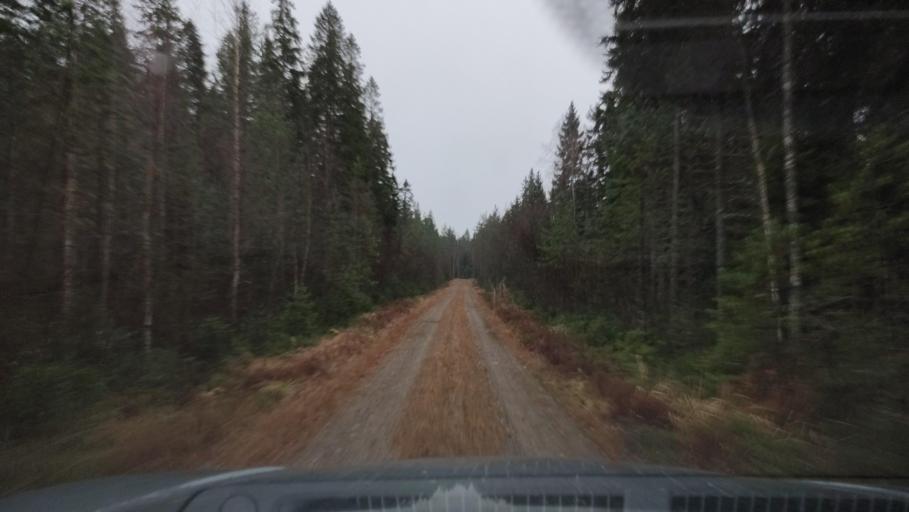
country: FI
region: Southern Ostrobothnia
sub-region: Suupohja
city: Karijoki
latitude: 62.1476
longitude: 21.5922
